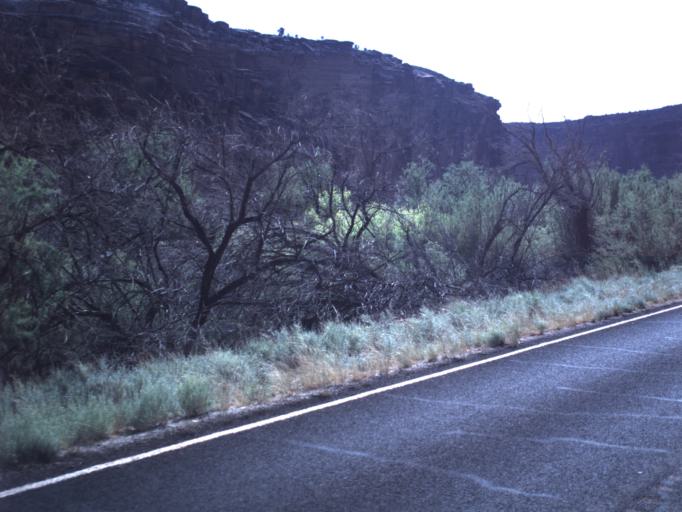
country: US
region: Utah
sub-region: Grand County
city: Moab
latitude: 38.5759
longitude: -109.6505
